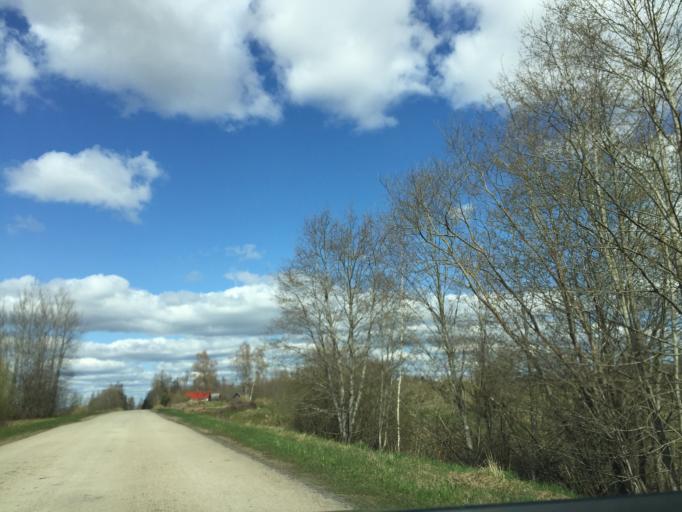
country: LV
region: Rezekne
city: Rezekne
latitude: 56.6697
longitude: 27.2020
